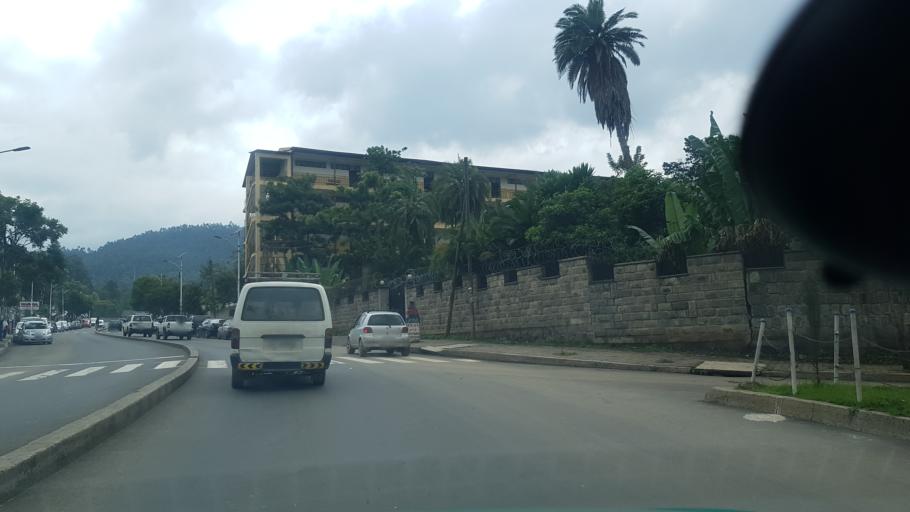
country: ET
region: Adis Abeba
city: Addis Ababa
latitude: 9.0284
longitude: 38.7846
